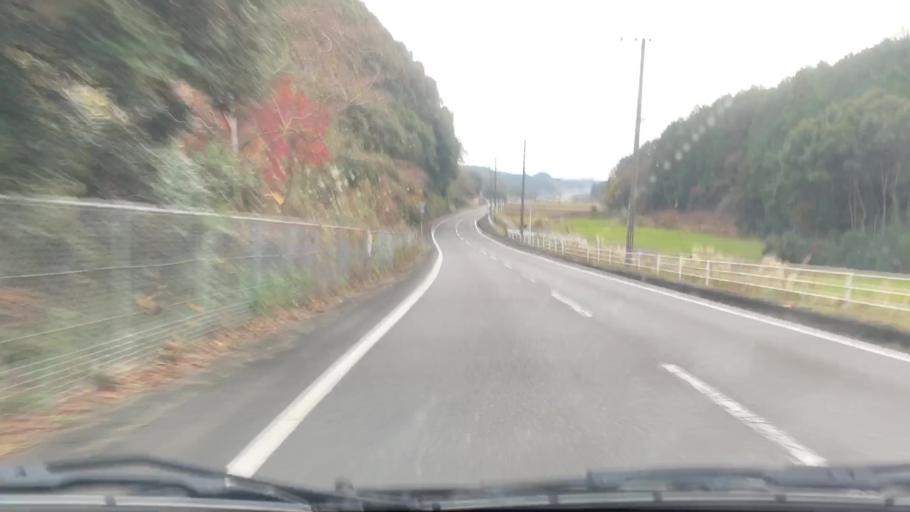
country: JP
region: Saga Prefecture
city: Ureshinomachi-shimojuku
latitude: 33.1164
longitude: 129.9769
